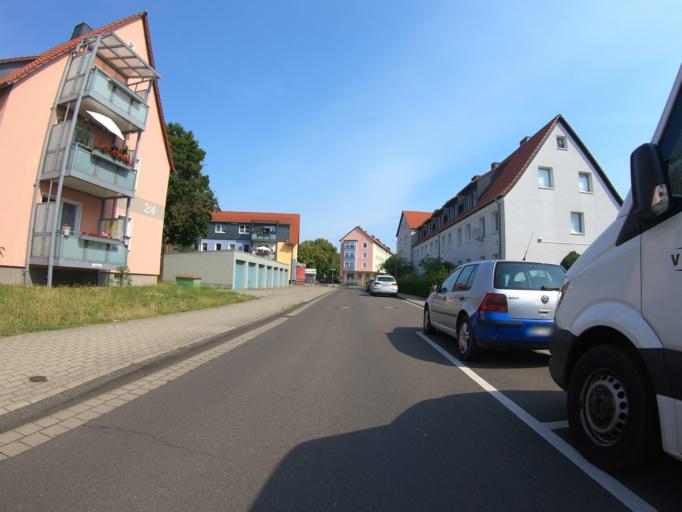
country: DE
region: Lower Saxony
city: Gifhorn
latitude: 52.4659
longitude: 10.5474
